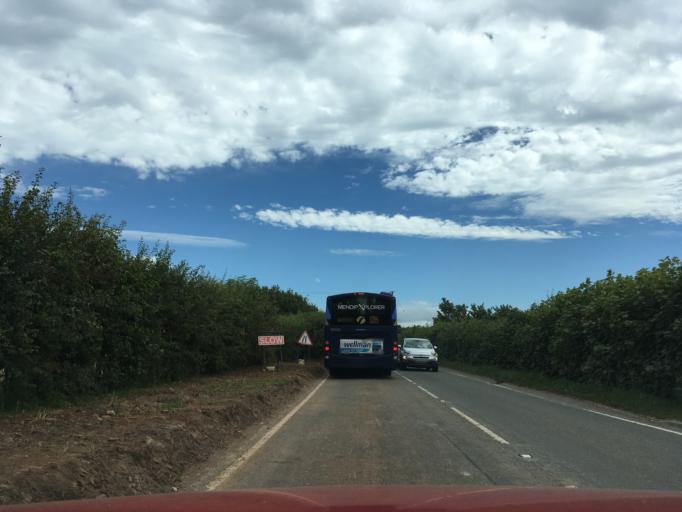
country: GB
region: England
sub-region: Somerset
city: Bradley Cross
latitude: 51.2660
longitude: -2.7664
